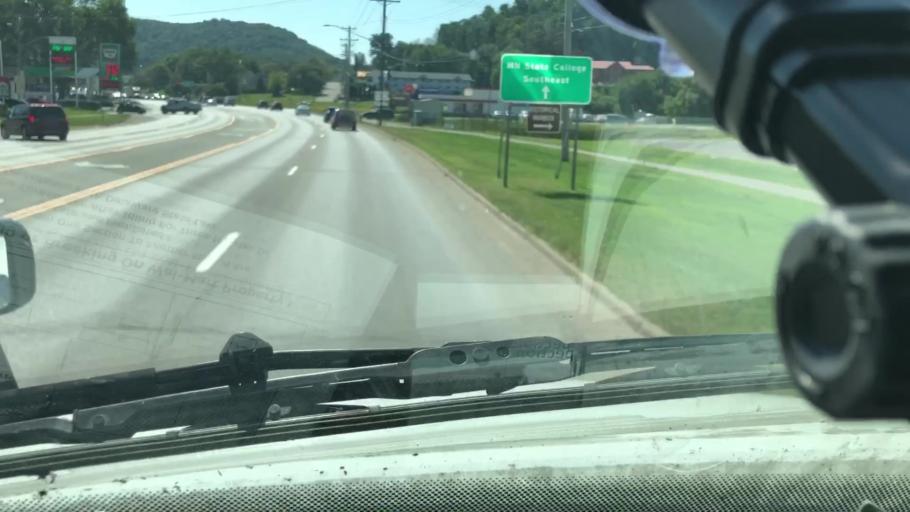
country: US
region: Minnesota
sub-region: Winona County
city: Winona
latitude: 44.0320
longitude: -91.6225
